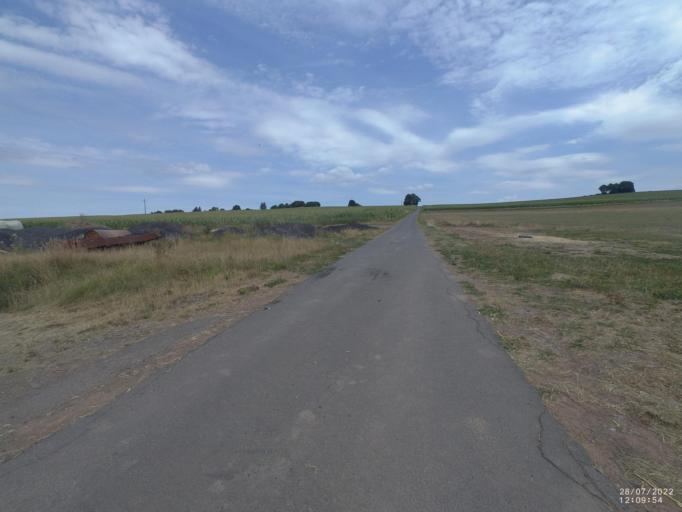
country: DE
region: Rheinland-Pfalz
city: Kalenborn-Scheuern
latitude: 50.2545
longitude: 6.6265
